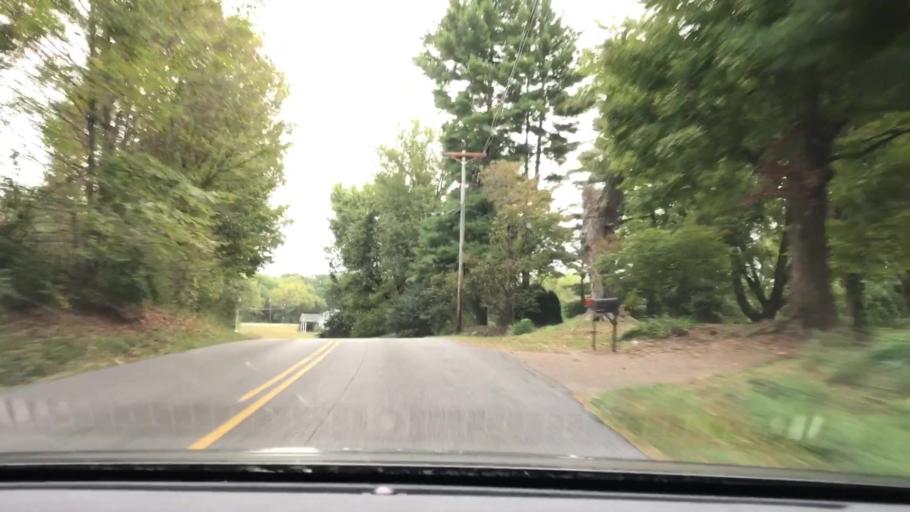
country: US
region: Kentucky
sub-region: Christian County
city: Hopkinsville
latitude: 36.8405
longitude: -87.5214
